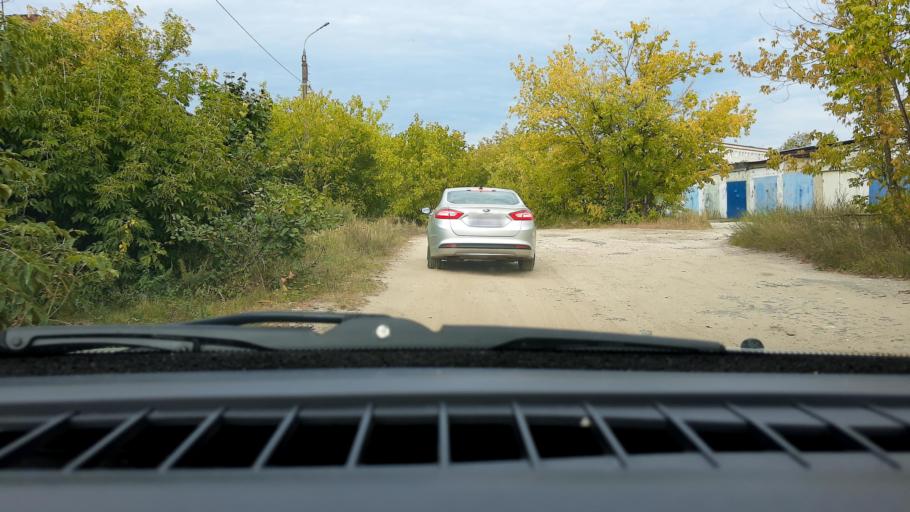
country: RU
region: Nizjnij Novgorod
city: Dzerzhinsk
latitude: 56.2477
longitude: 43.4800
